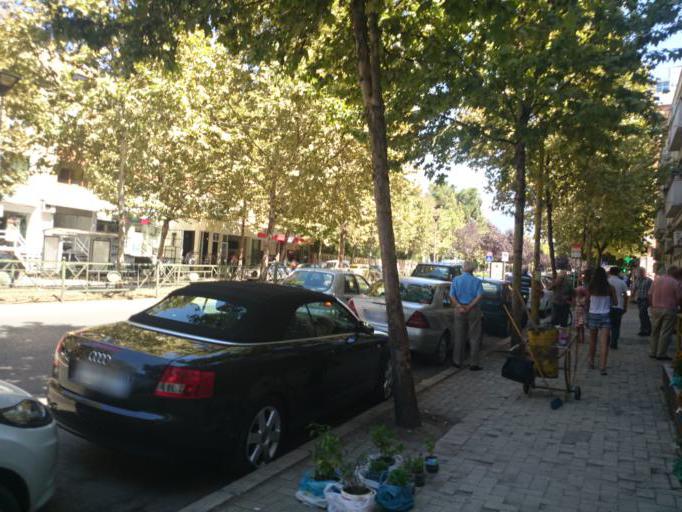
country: AL
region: Tirane
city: Tirana
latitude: 41.3261
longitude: 19.8048
